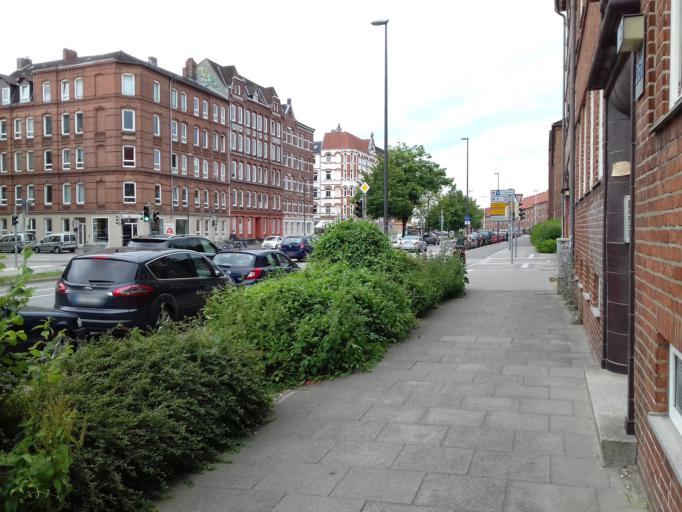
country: DE
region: Schleswig-Holstein
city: Kiel
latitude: 54.3263
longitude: 10.1154
